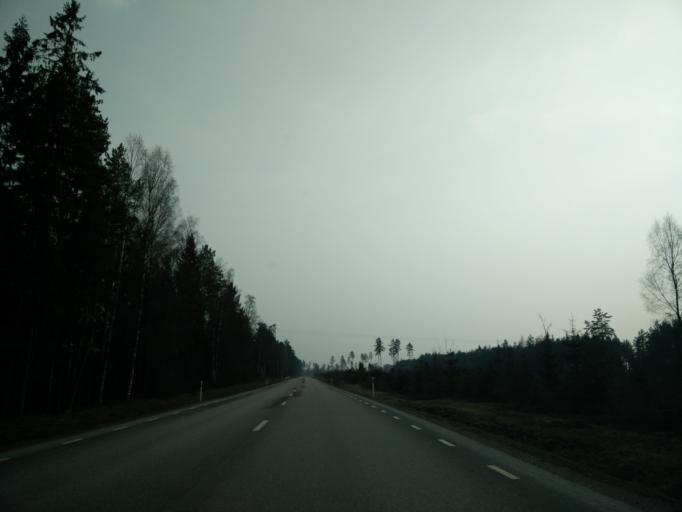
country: SE
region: Vaermland
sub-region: Forshaga Kommun
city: Forshaga
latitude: 59.5075
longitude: 13.4365
